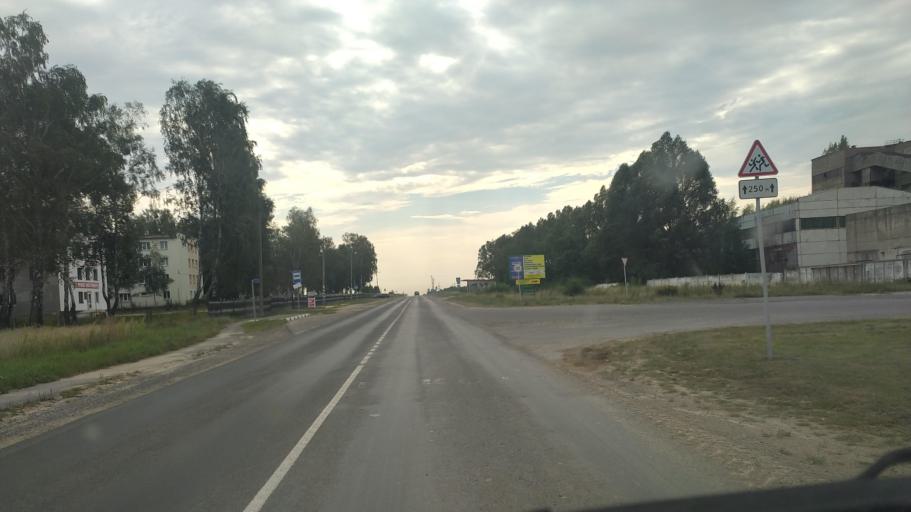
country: BY
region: Brest
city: Byaroza
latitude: 52.5518
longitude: 24.9351
